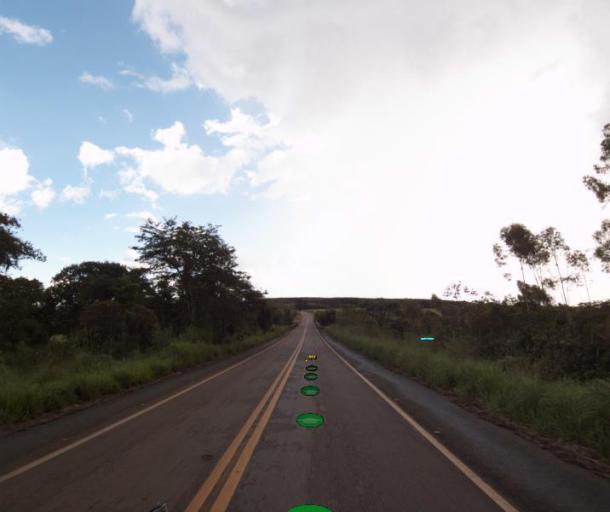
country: BR
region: Goias
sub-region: Itaberai
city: Itaberai
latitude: -15.9993
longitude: -49.7460
